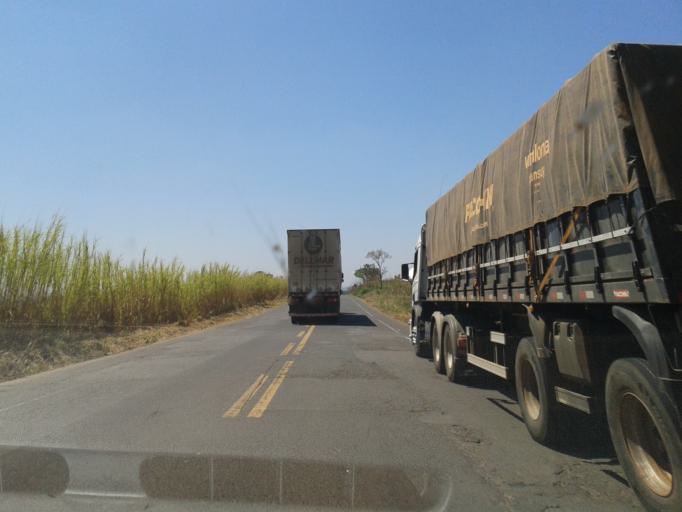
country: BR
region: Minas Gerais
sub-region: Araxa
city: Araxa
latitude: -19.4292
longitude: -47.2304
